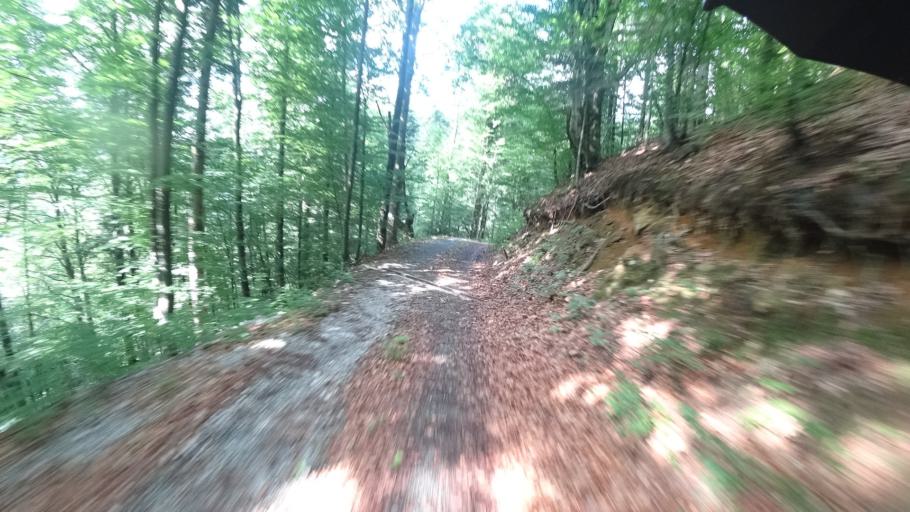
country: SI
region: Osilnica
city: Osilnica
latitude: 45.4712
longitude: 14.7011
